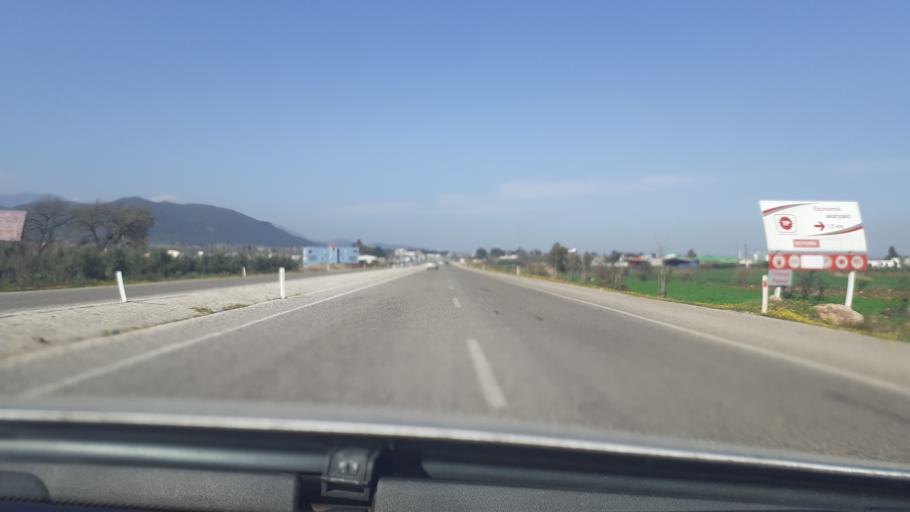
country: TR
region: Hatay
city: Aktepe
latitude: 36.6857
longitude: 36.4716
